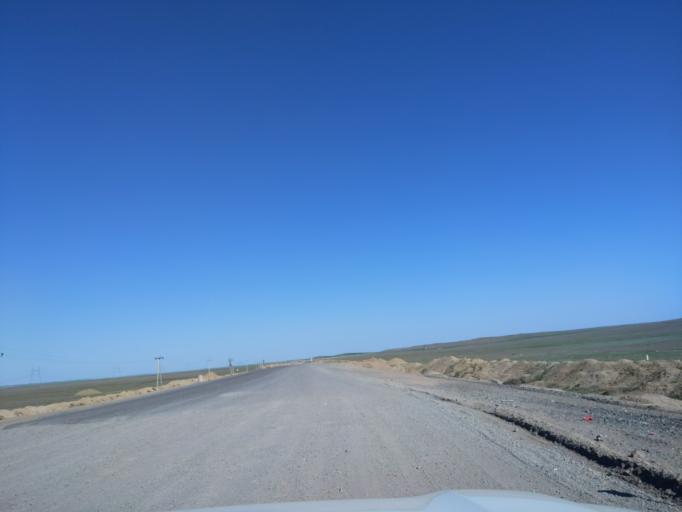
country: KZ
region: Almaty Oblysy
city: Bakanas
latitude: 44.0645
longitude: 76.0366
